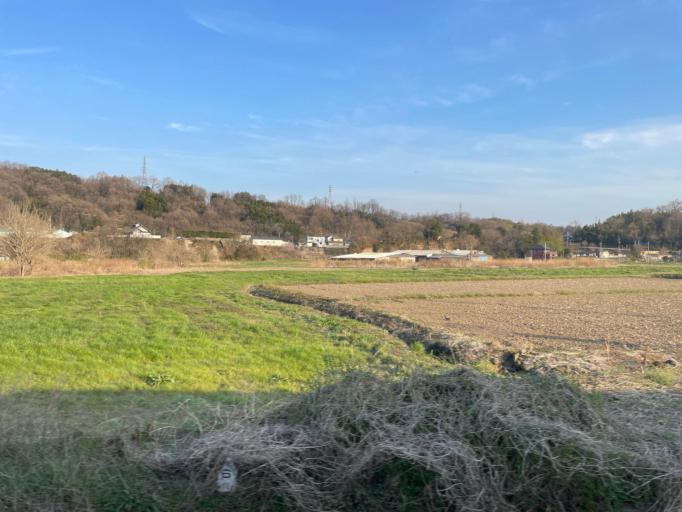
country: JP
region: Gunma
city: Annaka
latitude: 36.3268
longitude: 138.9043
